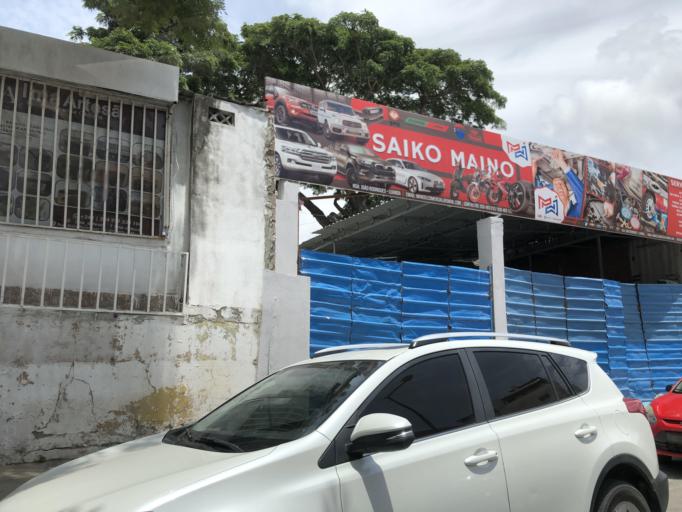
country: AO
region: Luanda
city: Luanda
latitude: -8.8218
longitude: 13.2309
